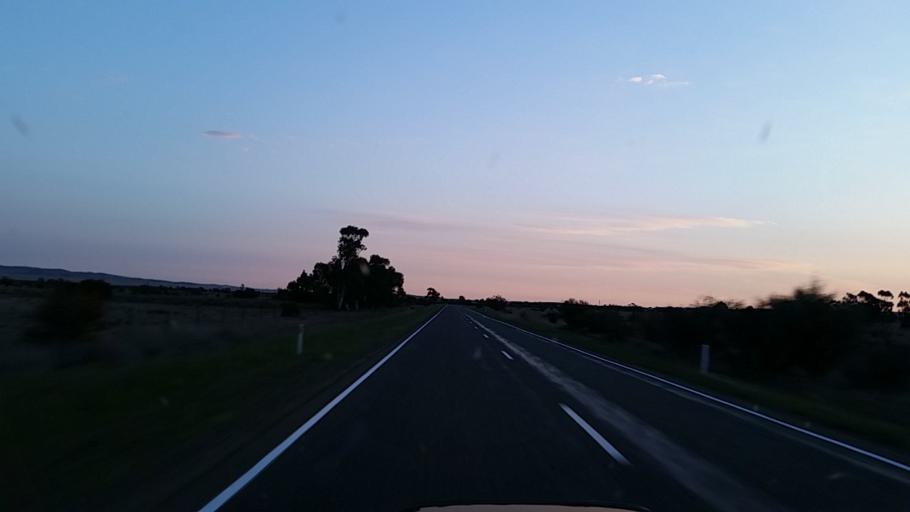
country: AU
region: South Australia
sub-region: Peterborough
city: Peterborough
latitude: -33.1404
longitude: 138.9313
